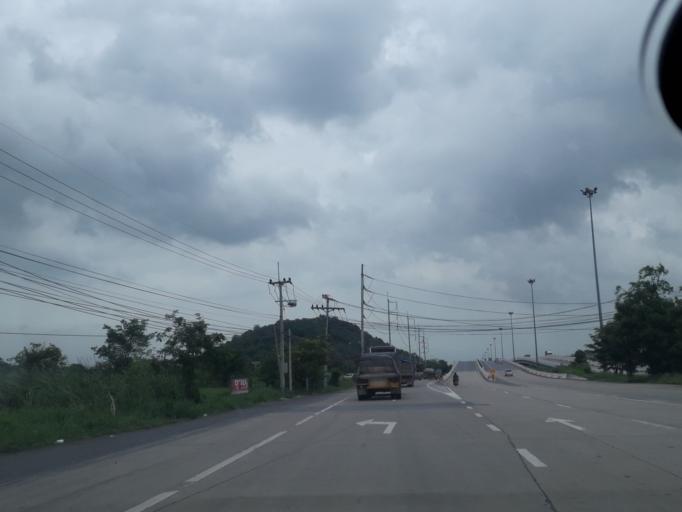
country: TH
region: Sara Buri
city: Saraburi
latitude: 14.5441
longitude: 100.9501
